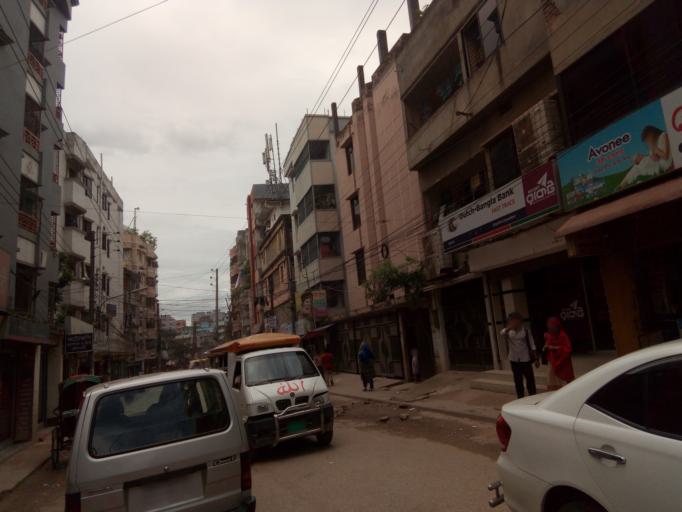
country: BD
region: Dhaka
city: Azimpur
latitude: 23.7590
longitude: 90.3593
